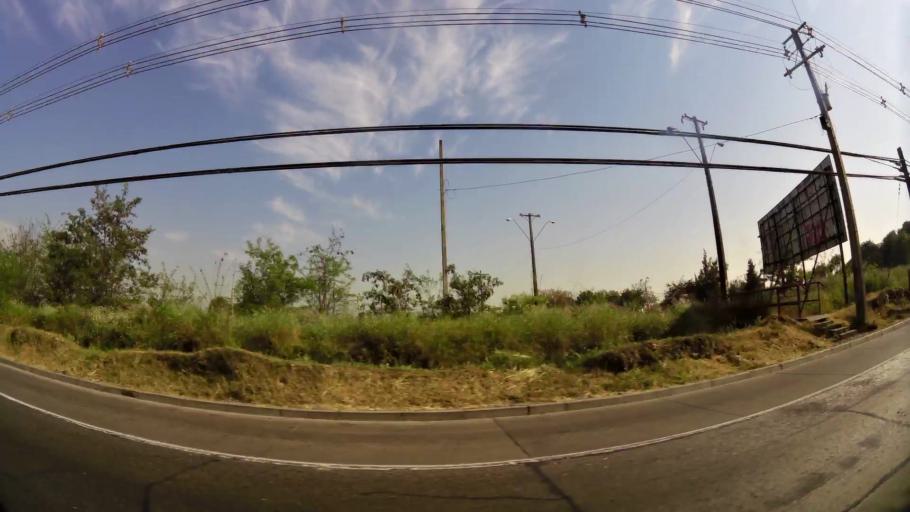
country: CL
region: Santiago Metropolitan
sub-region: Provincia de Maipo
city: San Bernardo
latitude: -33.5327
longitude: -70.7649
